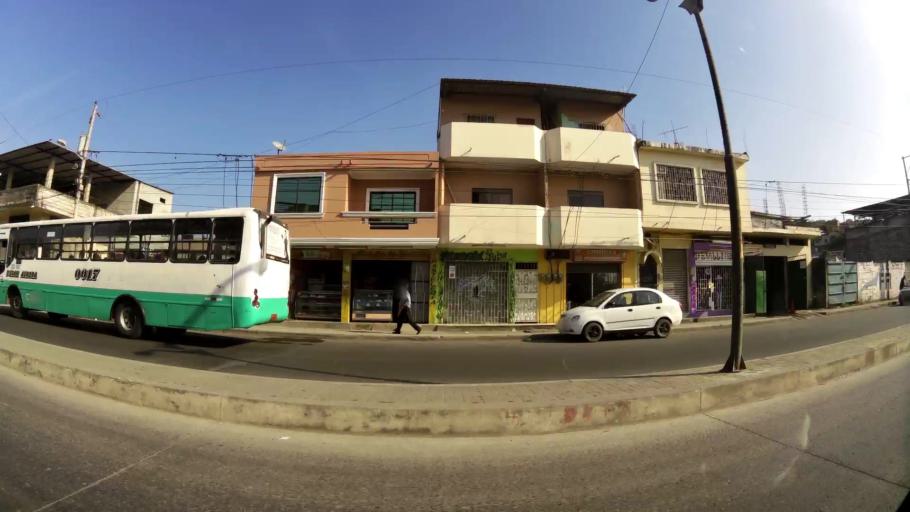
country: EC
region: Guayas
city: Eloy Alfaro
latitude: -2.1748
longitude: -79.8471
